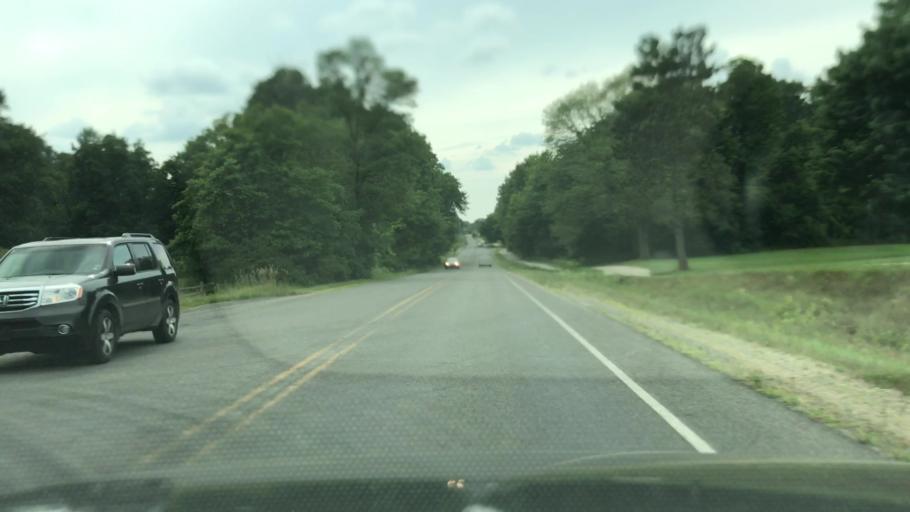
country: US
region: Michigan
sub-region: Kent County
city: East Grand Rapids
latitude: 42.9846
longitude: -85.5639
